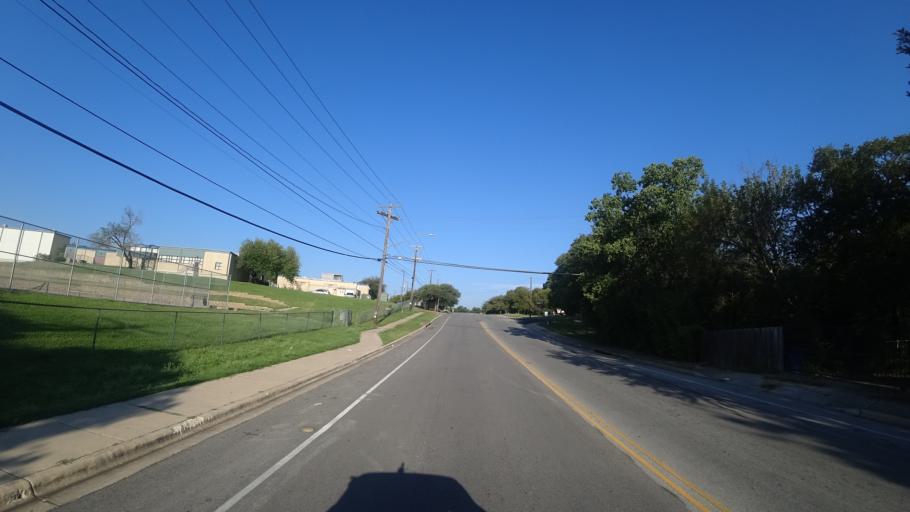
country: US
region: Texas
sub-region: Travis County
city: Austin
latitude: 30.3137
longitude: -97.6789
